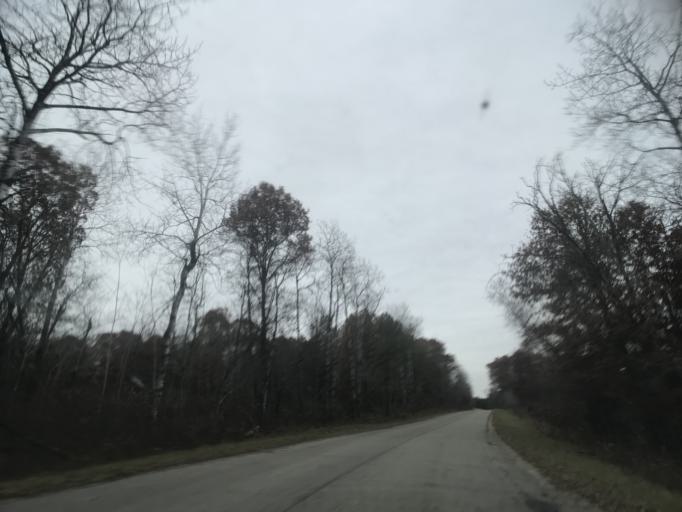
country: US
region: Wisconsin
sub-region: Oconto County
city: Gillett
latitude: 45.2975
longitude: -88.2550
